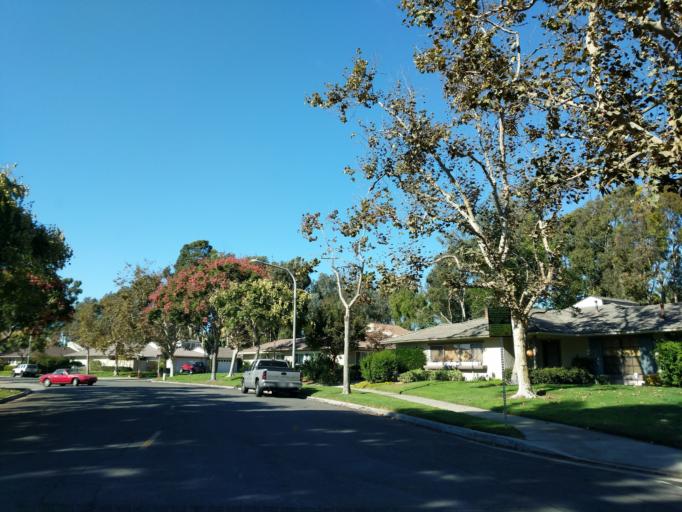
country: US
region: California
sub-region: Orange County
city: Irvine
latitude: 33.6621
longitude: -117.7979
